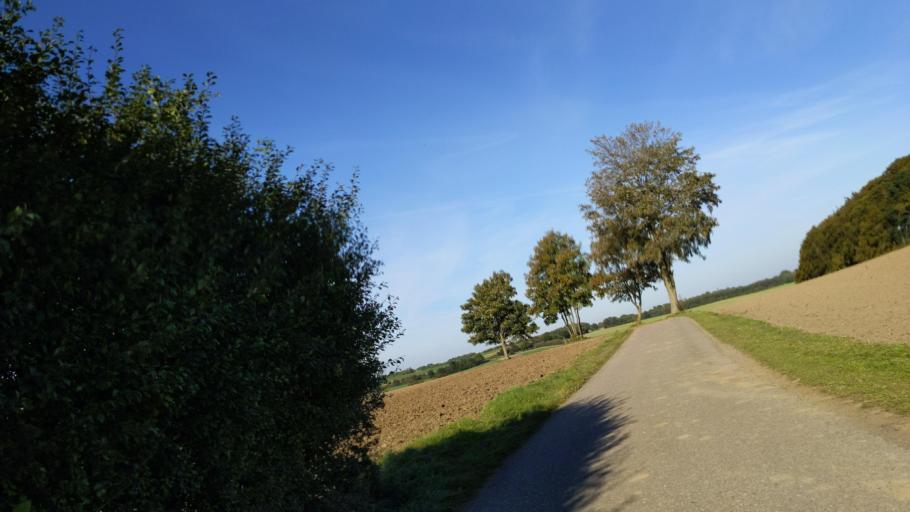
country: DE
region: Schleswig-Holstein
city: Ahrensbok
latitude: 54.0604
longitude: 10.5850
